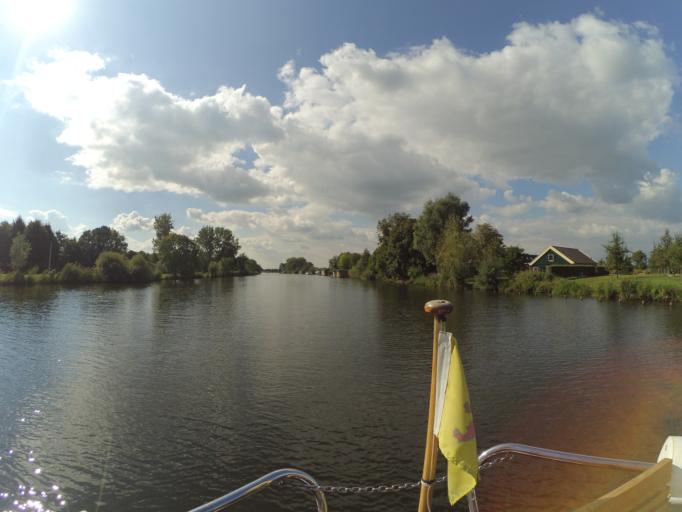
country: NL
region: Utrecht
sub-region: Stichtse Vecht
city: Vreeland
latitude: 52.2418
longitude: 5.0409
